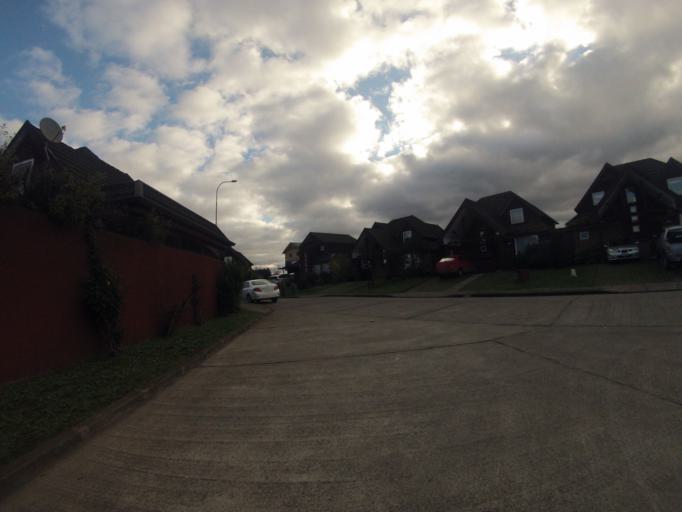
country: CL
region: Araucania
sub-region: Provincia de Cautin
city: Temuco
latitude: -38.7351
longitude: -72.6480
